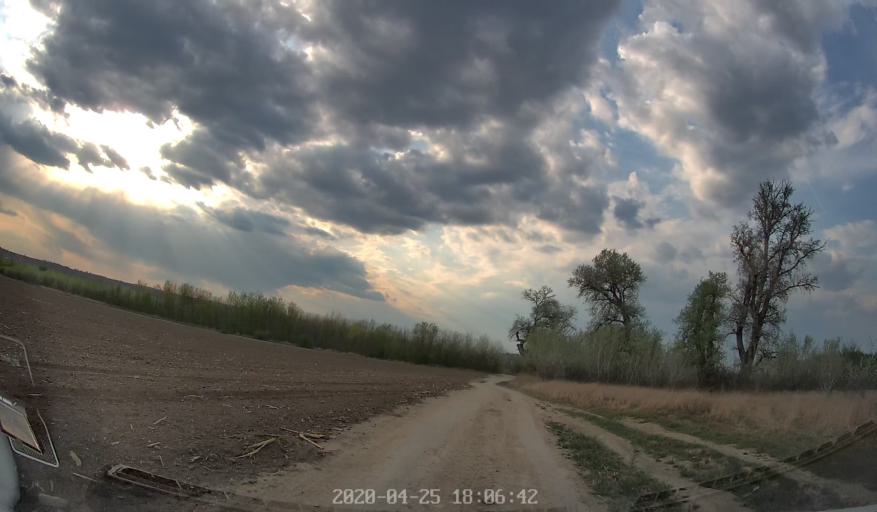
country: MD
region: Chisinau
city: Vadul lui Voda
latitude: 47.1281
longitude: 29.0842
